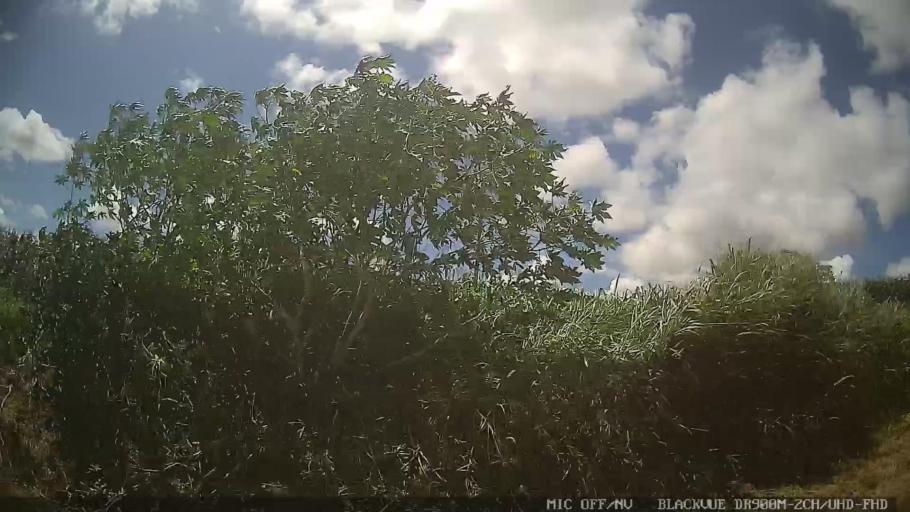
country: BR
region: Sao Paulo
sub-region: Amparo
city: Amparo
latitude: -22.8394
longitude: -46.7065
